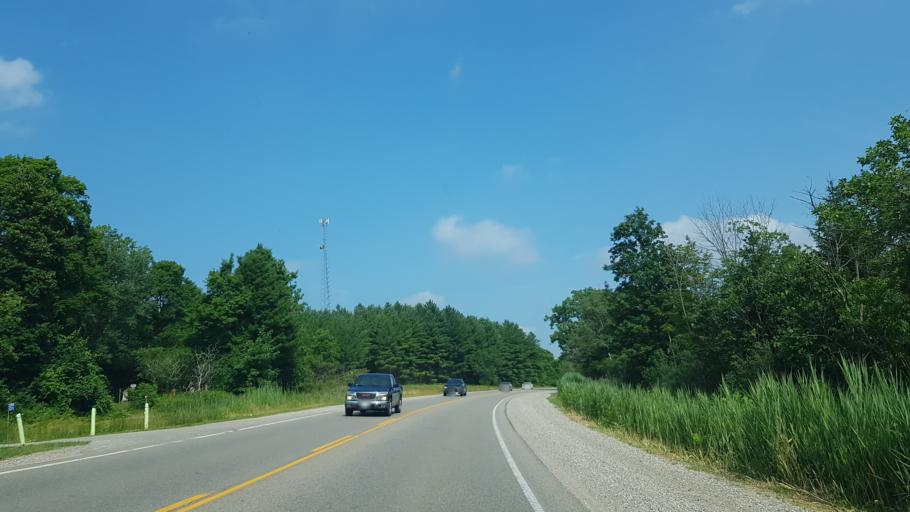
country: CA
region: Ontario
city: Delaware
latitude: 42.9651
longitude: -81.3785
